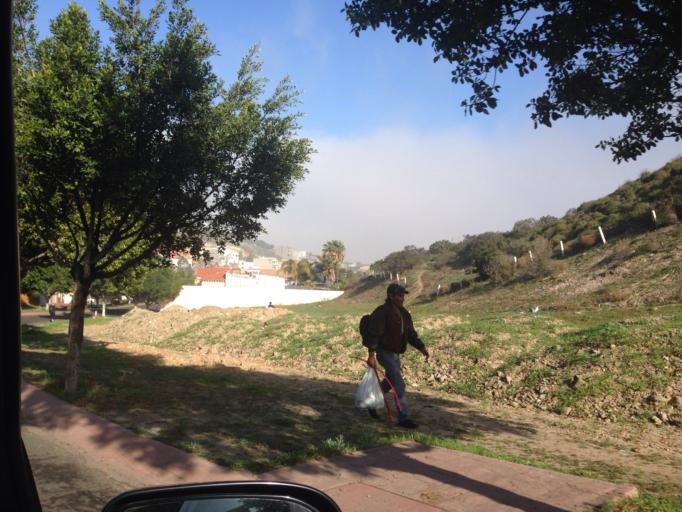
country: MX
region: Baja California
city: Tijuana
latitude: 32.4895
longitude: -117.0013
